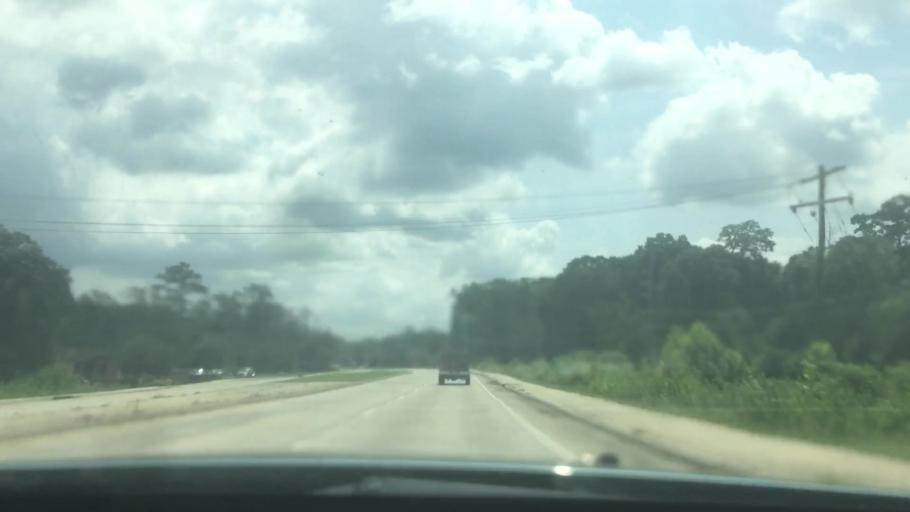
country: US
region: Louisiana
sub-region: East Baton Rouge Parish
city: Shenandoah
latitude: 30.4252
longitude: -91.0131
